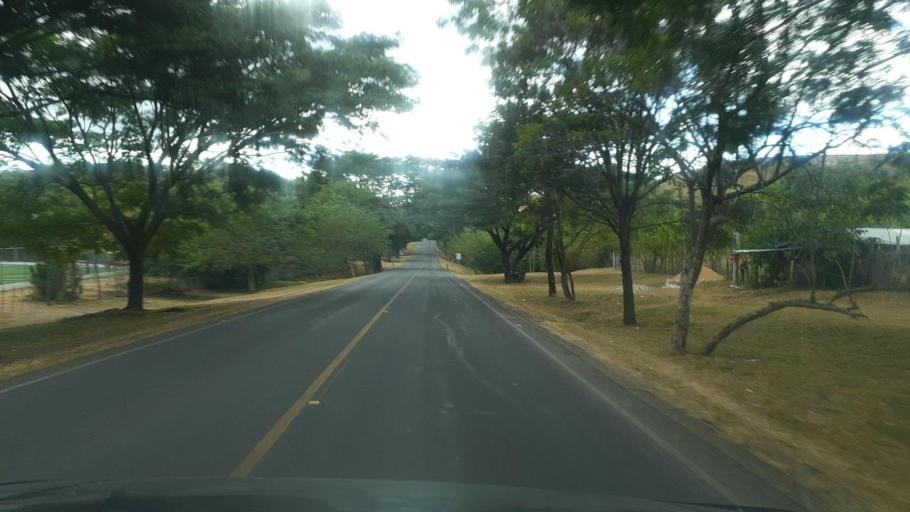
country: NI
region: Madriz
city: Somoto
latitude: 13.4766
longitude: -86.5939
